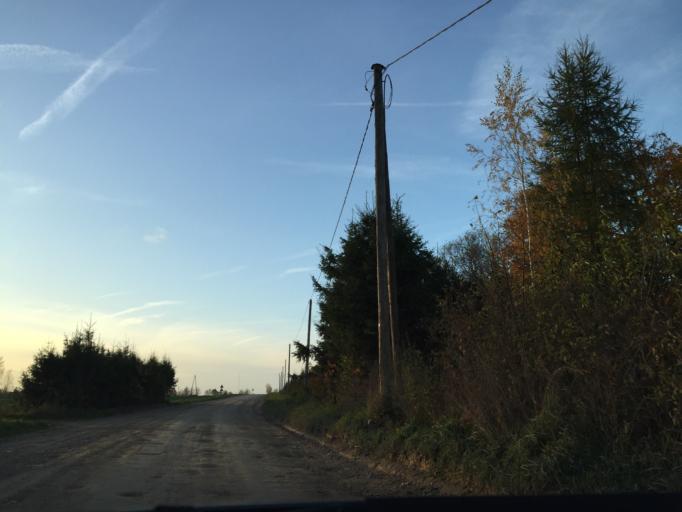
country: LV
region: Malpils
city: Malpils
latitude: 56.8836
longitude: 24.9664
